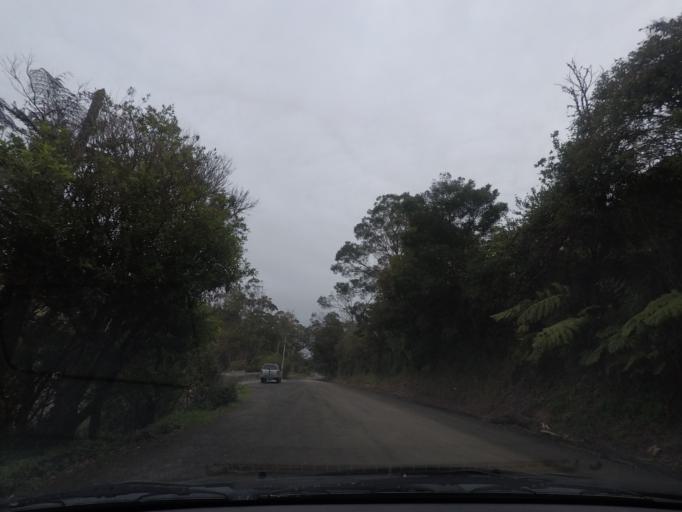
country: NZ
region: Auckland
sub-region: Auckland
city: Muriwai Beach
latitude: -36.7525
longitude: 174.5753
